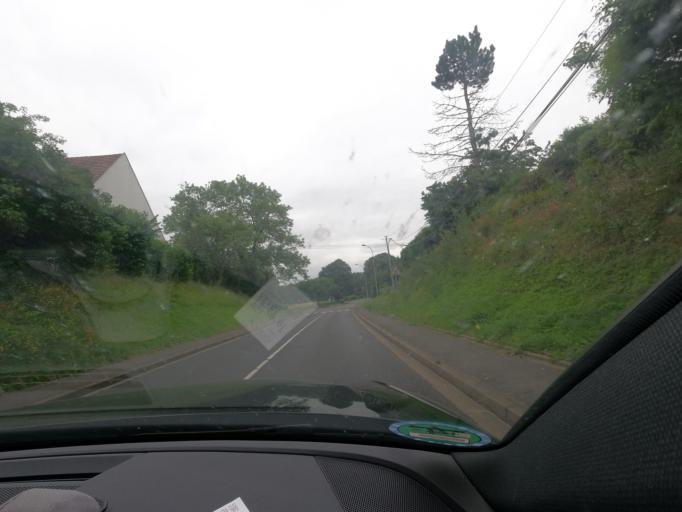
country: FR
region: Picardie
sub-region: Departement de l'Oise
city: Ressons-sur-Matz
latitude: 49.5365
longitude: 2.7423
